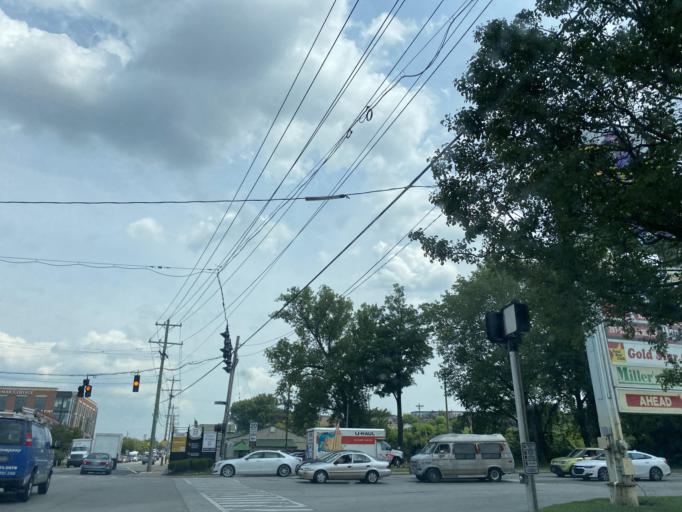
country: US
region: Kentucky
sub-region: Campbell County
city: Bellevue
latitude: 39.1016
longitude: -84.4888
